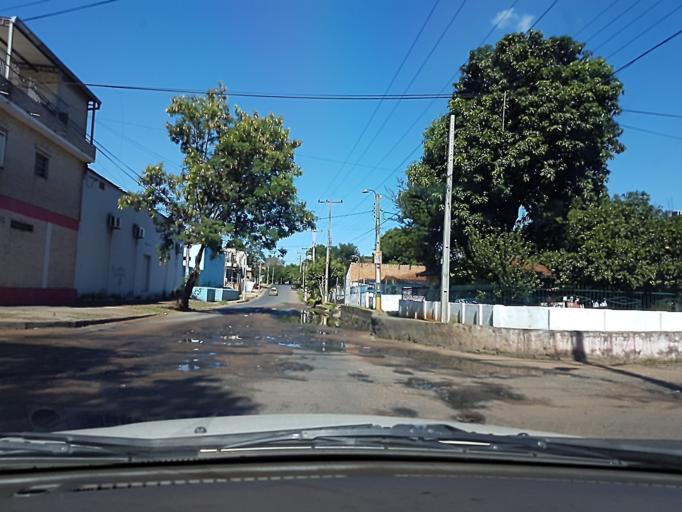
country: PY
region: Central
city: Lambare
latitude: -25.3214
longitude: -57.5891
